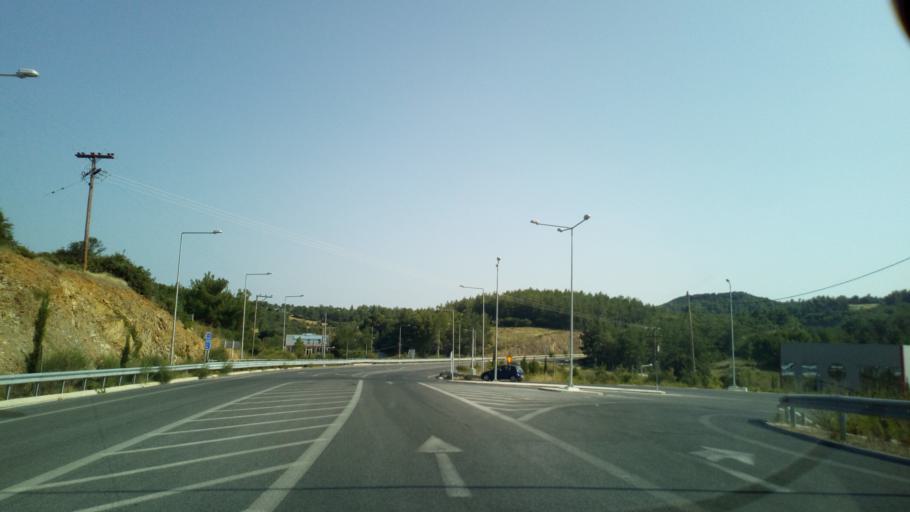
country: GR
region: Central Macedonia
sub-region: Nomos Chalkidikis
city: Polygyros
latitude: 40.3654
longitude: 23.4401
